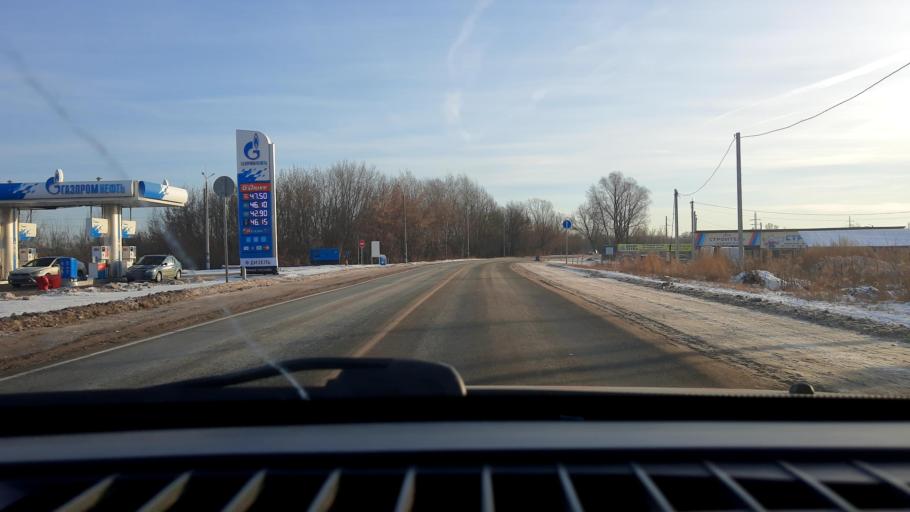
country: RU
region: Nizjnij Novgorod
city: Bor
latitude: 56.3774
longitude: 44.0554
